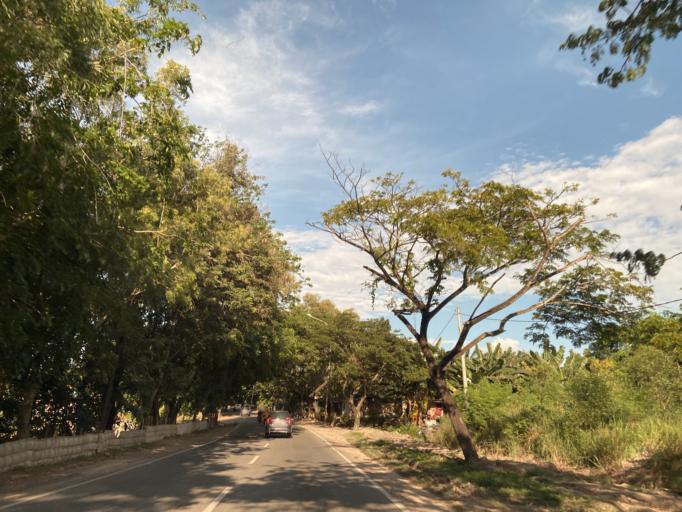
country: SG
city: Singapore
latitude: 1.1225
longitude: 104.0123
